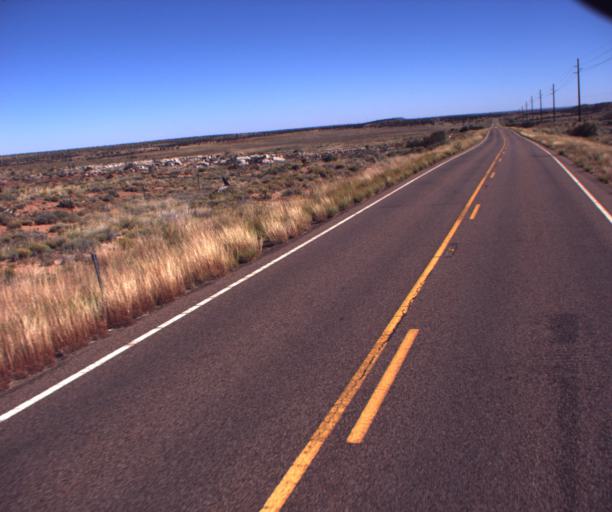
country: US
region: Arizona
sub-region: Navajo County
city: Taylor
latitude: 34.4986
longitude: -110.1996
